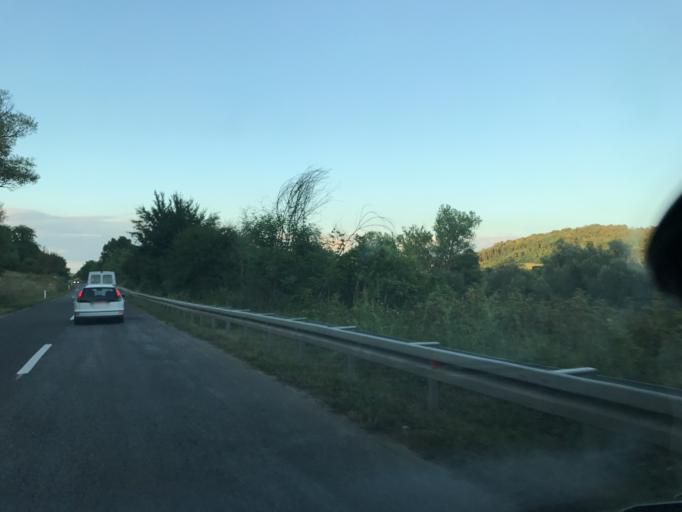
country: RS
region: Central Serbia
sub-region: Branicevski Okrug
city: Veliko Gradiste
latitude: 44.7059
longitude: 21.3825
